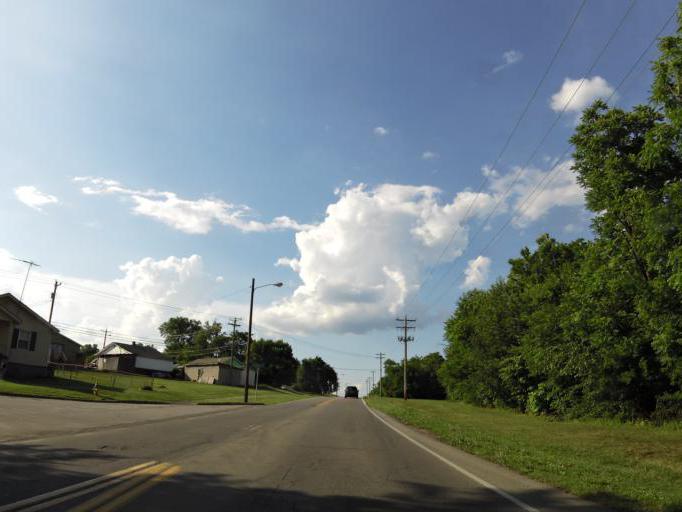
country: US
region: Tennessee
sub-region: Blount County
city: Alcoa
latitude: 35.7749
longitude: -83.9771
